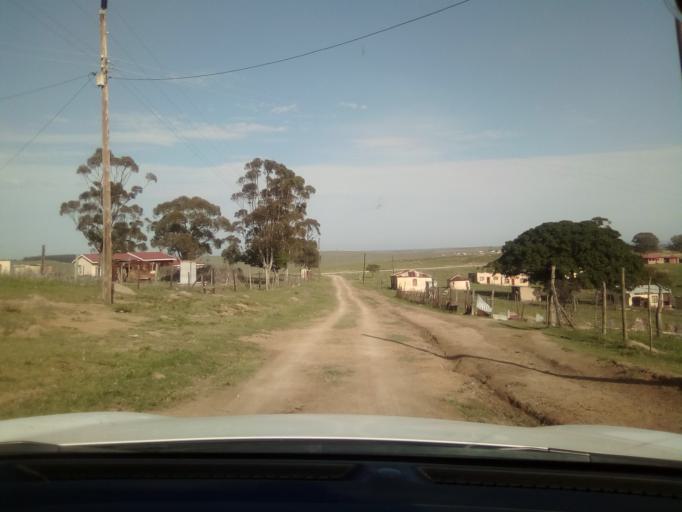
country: ZA
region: Eastern Cape
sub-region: Buffalo City Metropolitan Municipality
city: Bhisho
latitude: -32.9854
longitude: 27.2578
